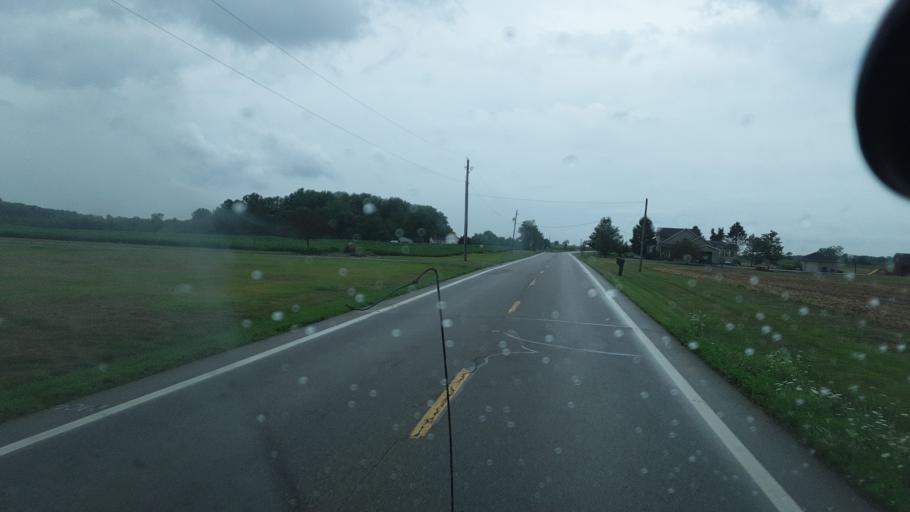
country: US
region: Indiana
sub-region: Steuben County
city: Hamilton
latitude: 41.5564
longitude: -84.7997
